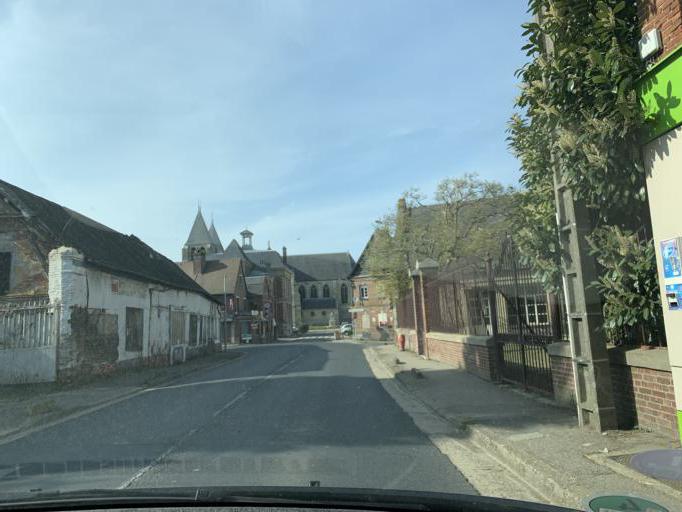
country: FR
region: Haute-Normandie
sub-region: Departement de l'Eure
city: Les Andelys
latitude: 49.3097
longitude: 1.4336
